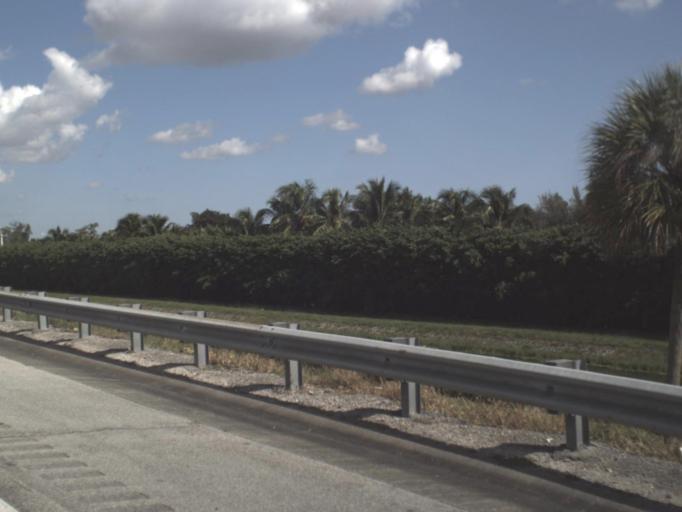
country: US
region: Florida
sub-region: Palm Beach County
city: Boca Del Mar
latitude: 26.3655
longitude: -80.1707
